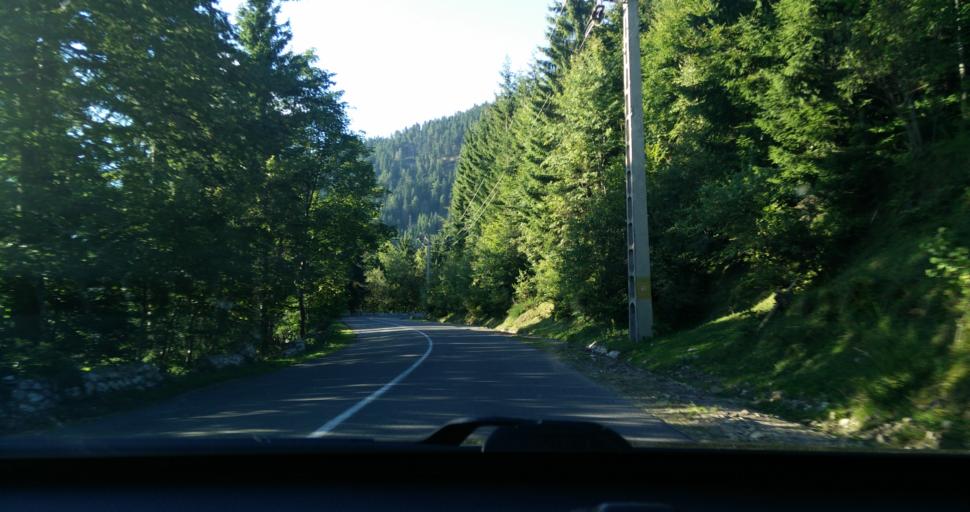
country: RO
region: Bihor
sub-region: Oras Nucet
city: Nucet
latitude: 46.5165
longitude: 22.6442
